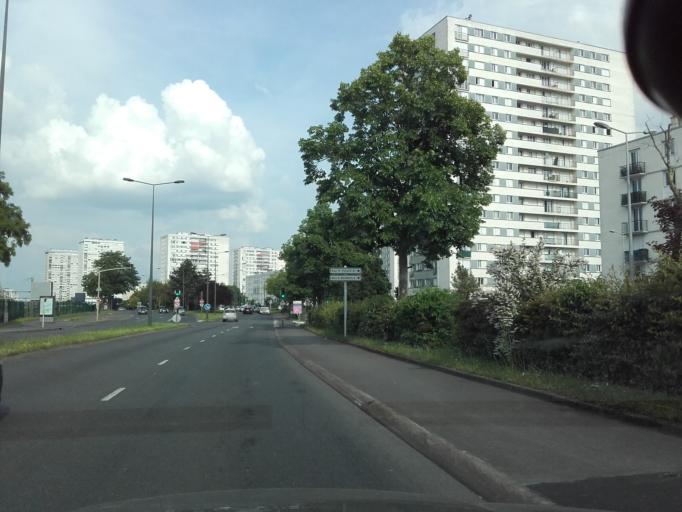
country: FR
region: Centre
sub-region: Departement d'Indre-et-Loire
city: Tours
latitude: 47.3735
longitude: 0.6860
